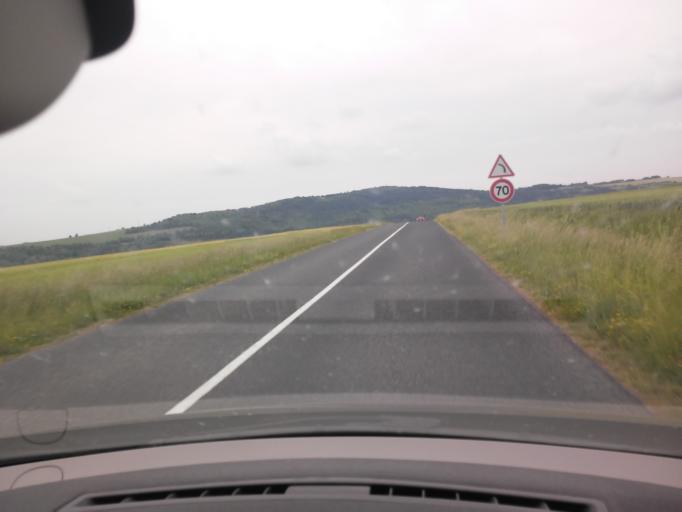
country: FR
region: Lorraine
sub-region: Departement de la Meuse
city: Saint-Mihiel
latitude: 48.8561
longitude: 5.5214
